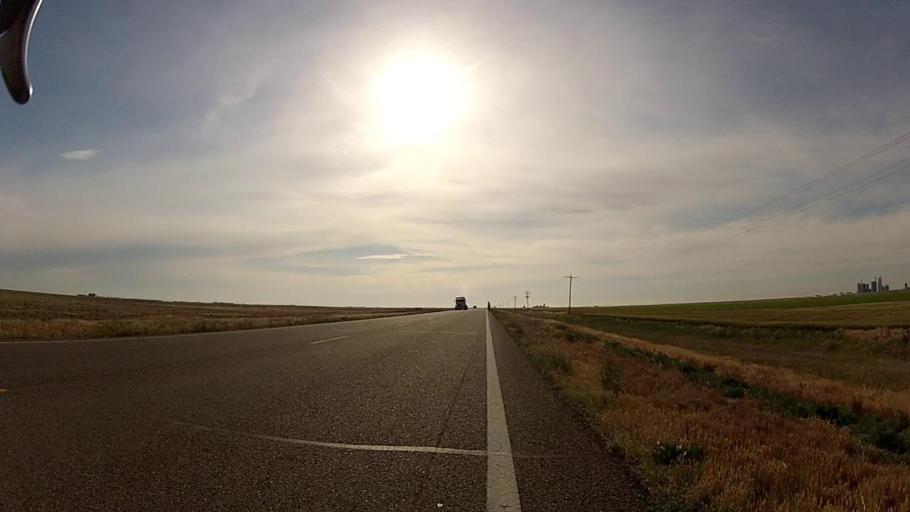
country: US
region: Kansas
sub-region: Grant County
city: Ulysses
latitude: 37.5766
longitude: -101.4692
